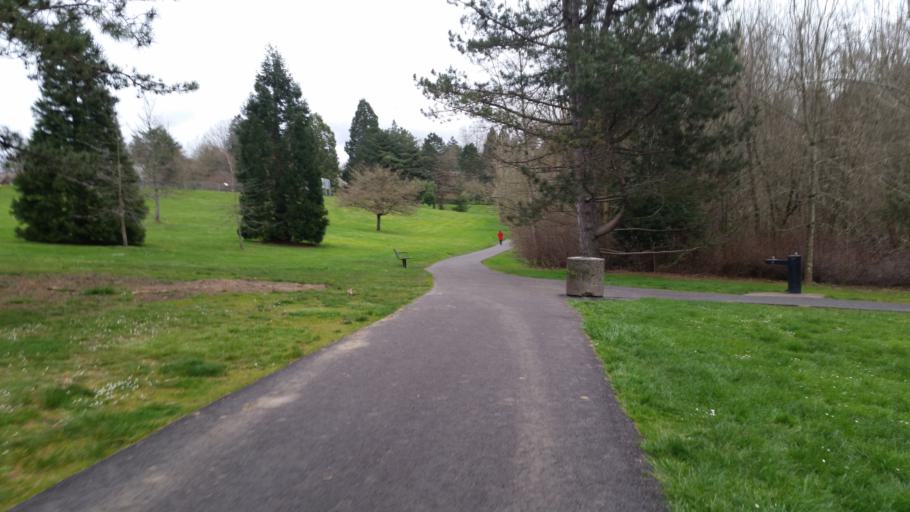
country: US
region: Oregon
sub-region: Washington County
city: Garden Home-Whitford
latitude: 45.4735
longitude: -122.7183
